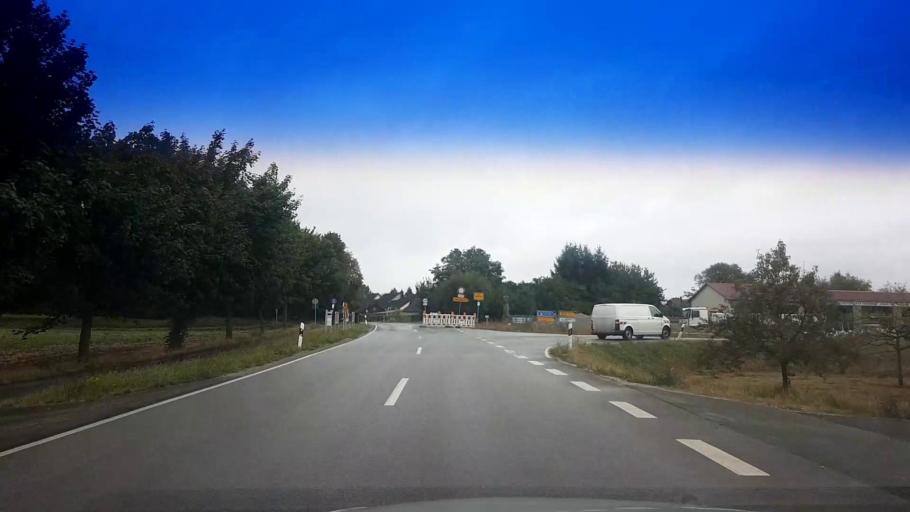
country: DE
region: Bavaria
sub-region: Upper Franconia
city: Eggolsheim
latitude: 49.7757
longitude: 11.0511
